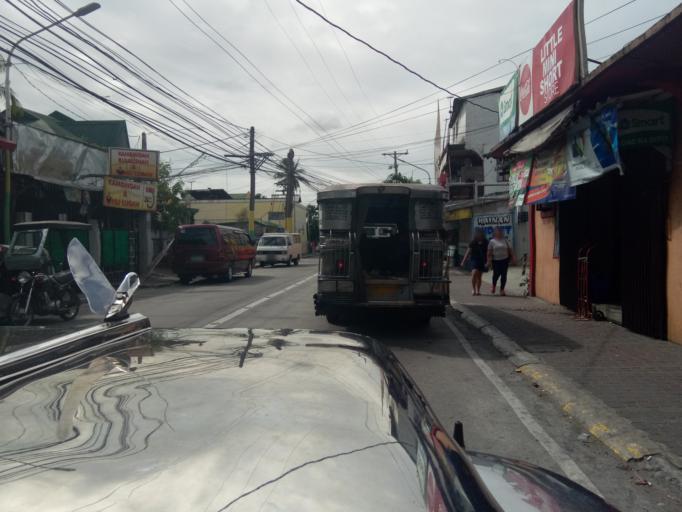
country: PH
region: Calabarzon
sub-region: Province of Cavite
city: Dasmarinas
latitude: 14.3189
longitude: 120.9413
